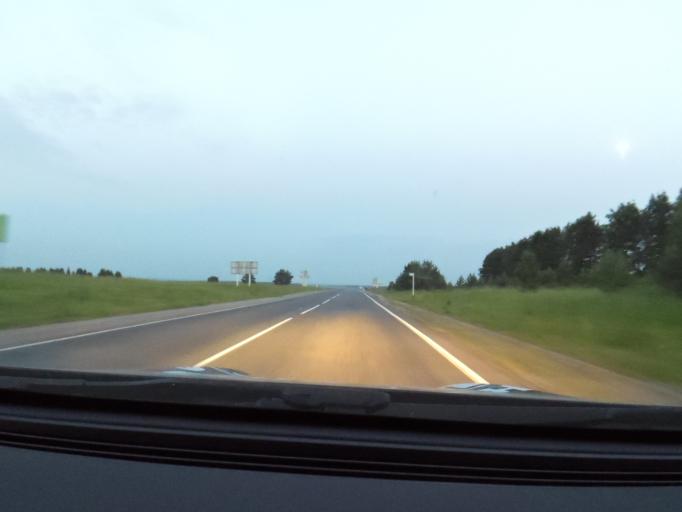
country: RU
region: Bashkortostan
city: Duvan
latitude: 56.1143
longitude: 58.0482
